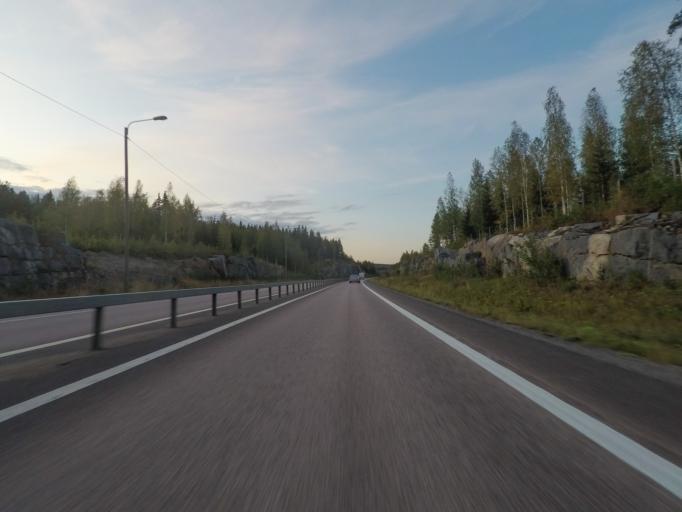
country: FI
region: Central Finland
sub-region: Jyvaeskylae
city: Saeynaetsalo
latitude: 62.2133
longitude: 25.8902
